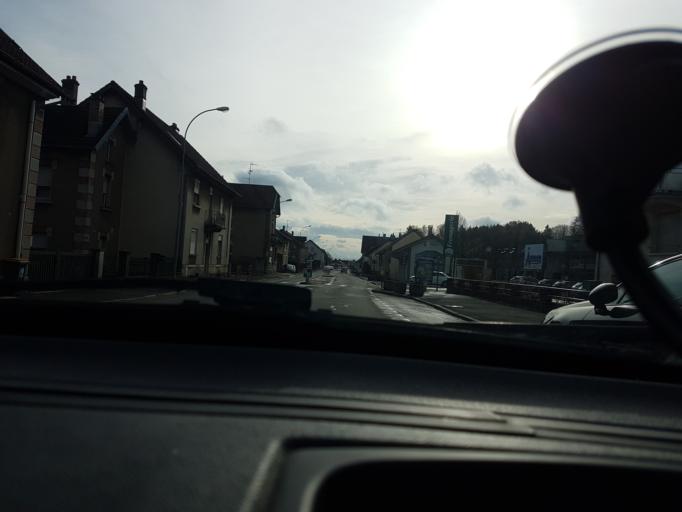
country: FR
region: Franche-Comte
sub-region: Territoire de Belfort
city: Danjoutin
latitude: 47.6150
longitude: 6.8596
